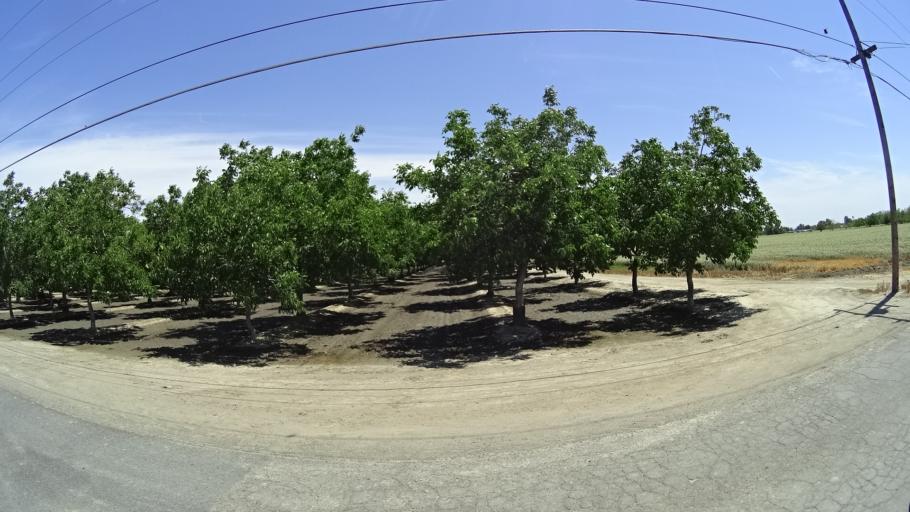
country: US
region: California
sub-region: Kings County
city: Armona
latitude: 36.3247
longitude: -119.7180
